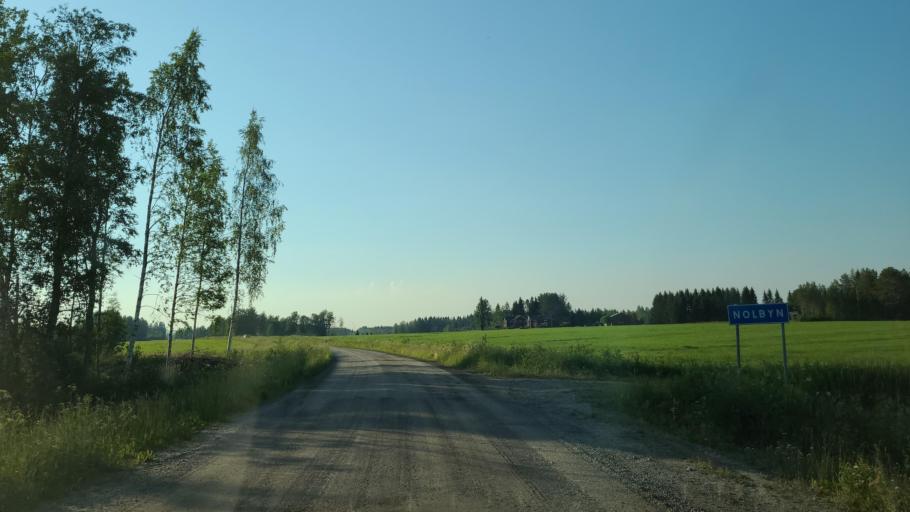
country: SE
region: Vaesterbotten
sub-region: Skelleftea Kommun
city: Burea
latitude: 64.3946
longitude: 21.3823
